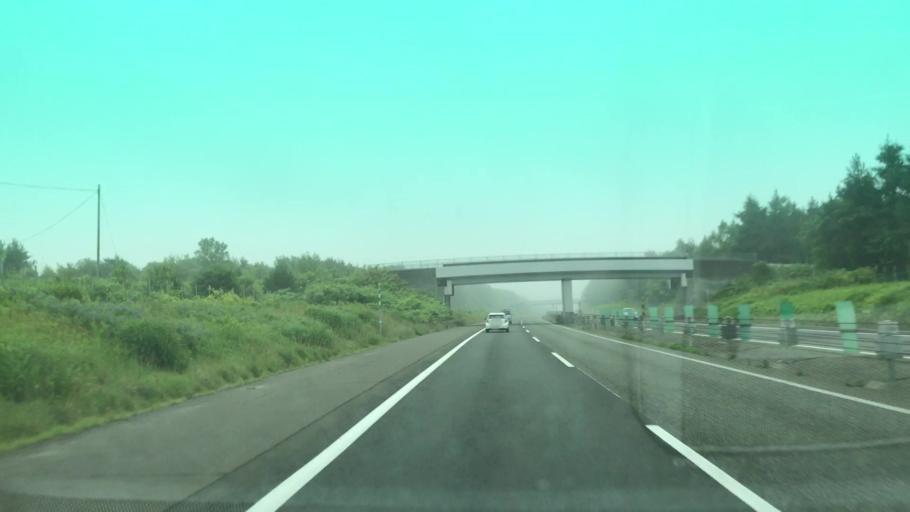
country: JP
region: Hokkaido
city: Chitose
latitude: 42.8274
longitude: 141.6142
